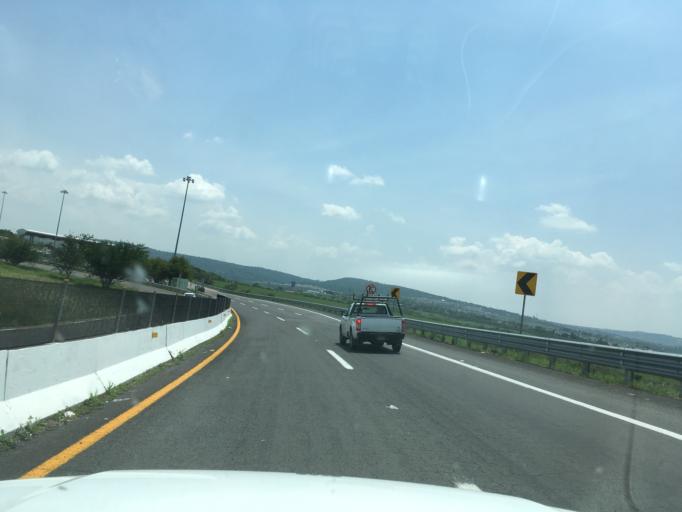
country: MX
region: Jalisco
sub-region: Tonala
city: Mismaloya (Fraccionamiento Pedregal de Santa Martha)
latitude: 20.6071
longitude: -103.1368
